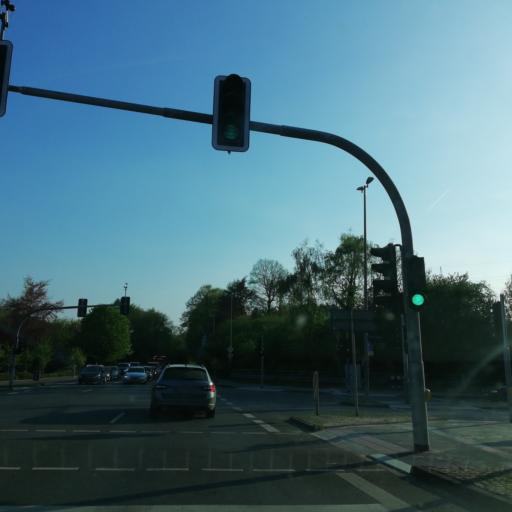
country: DE
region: North Rhine-Westphalia
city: Herdecke
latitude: 51.4198
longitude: 7.4360
